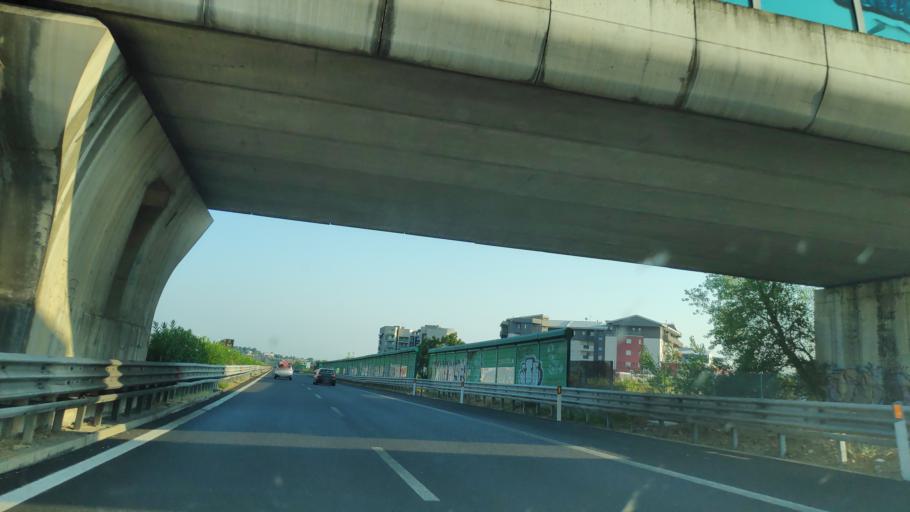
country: IT
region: Calabria
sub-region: Provincia di Cosenza
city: Quattromiglia
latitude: 39.3288
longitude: 16.2393
